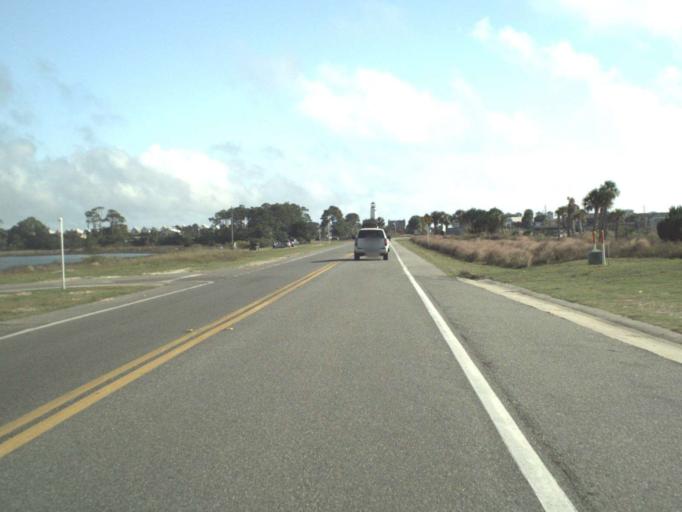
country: US
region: Florida
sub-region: Franklin County
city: Eastpoint
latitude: 29.6685
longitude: -84.8660
